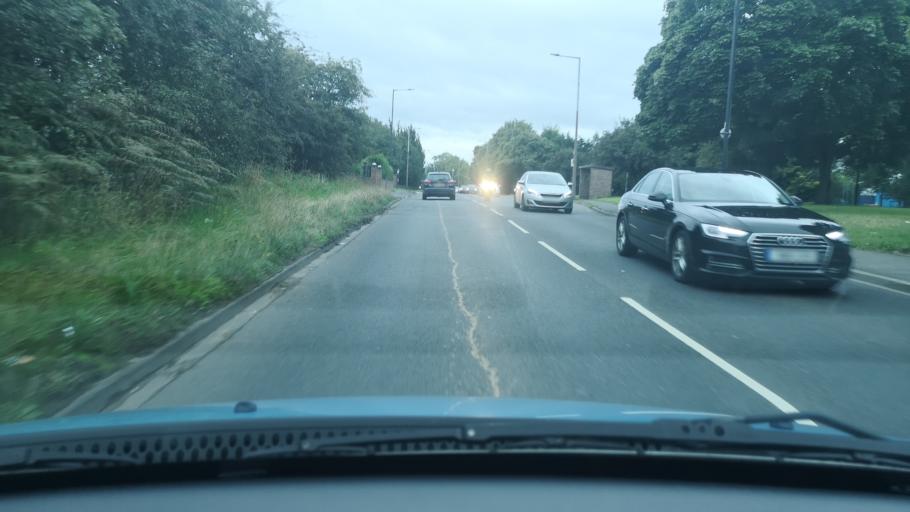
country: GB
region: England
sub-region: Doncaster
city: Kirk Sandall
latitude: 53.5524
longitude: -1.0842
